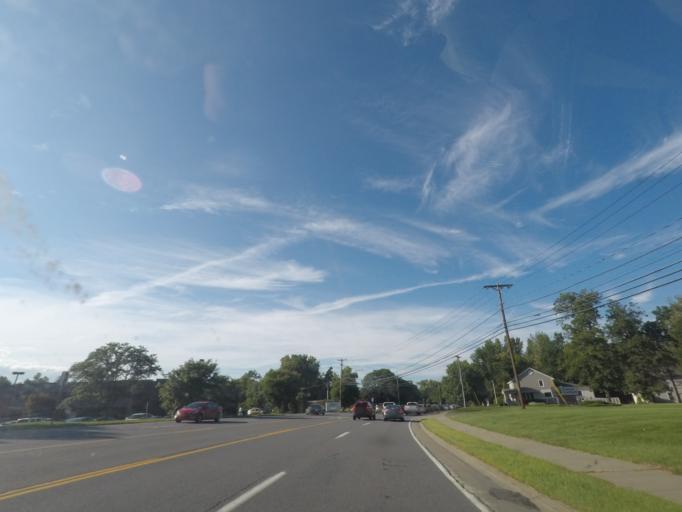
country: US
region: New York
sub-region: Schenectady County
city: Niskayuna
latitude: 42.7642
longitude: -73.8153
